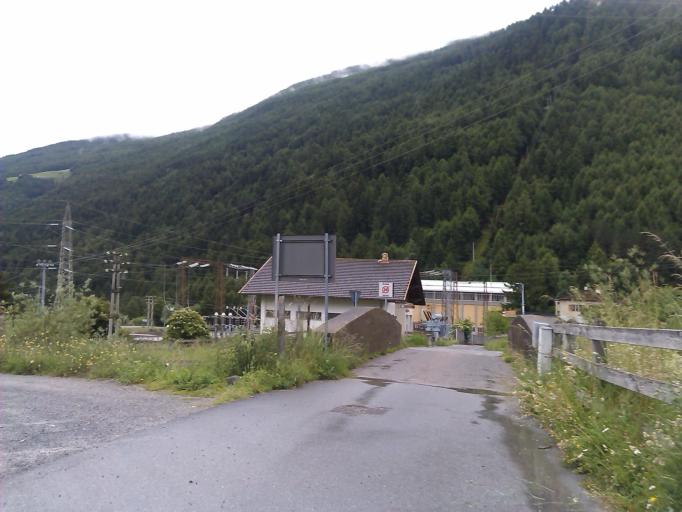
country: IT
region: Trentino-Alto Adige
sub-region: Bolzano
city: Lasa
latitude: 46.6125
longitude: 10.7069
